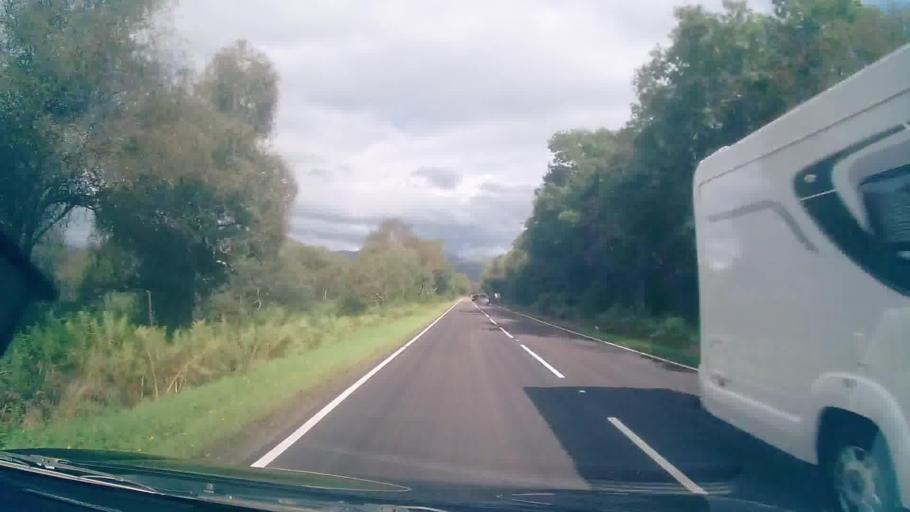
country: GB
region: Scotland
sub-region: Argyll and Bute
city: Oban
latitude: 56.4398
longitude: -5.2882
